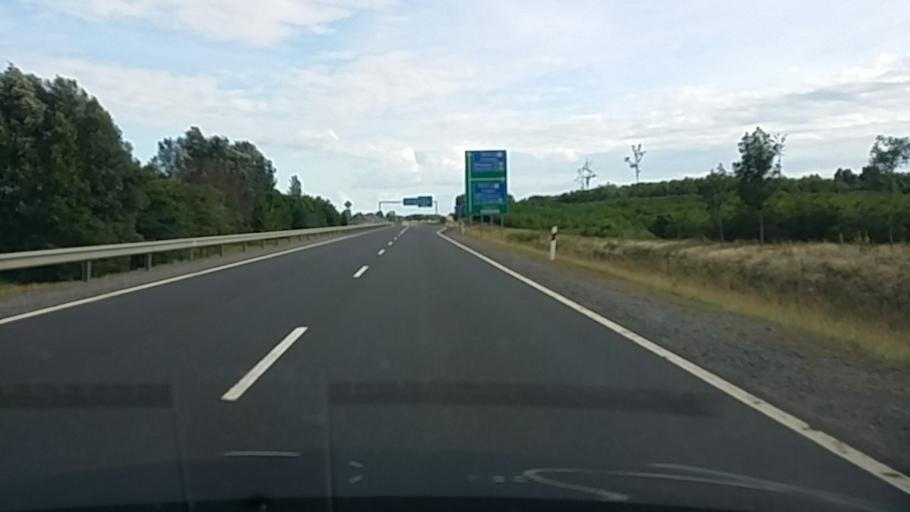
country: HU
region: Szabolcs-Szatmar-Bereg
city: Nagykallo
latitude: 47.9043
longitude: 21.8176
